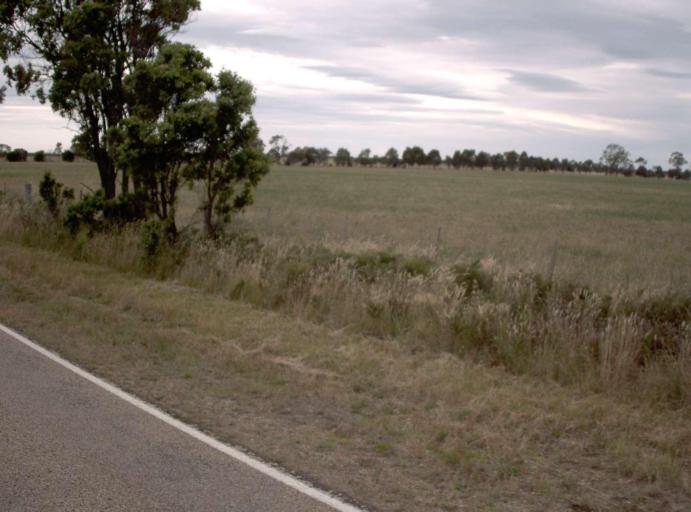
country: AU
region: Victoria
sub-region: East Gippsland
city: Bairnsdale
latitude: -37.9546
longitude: 147.5093
